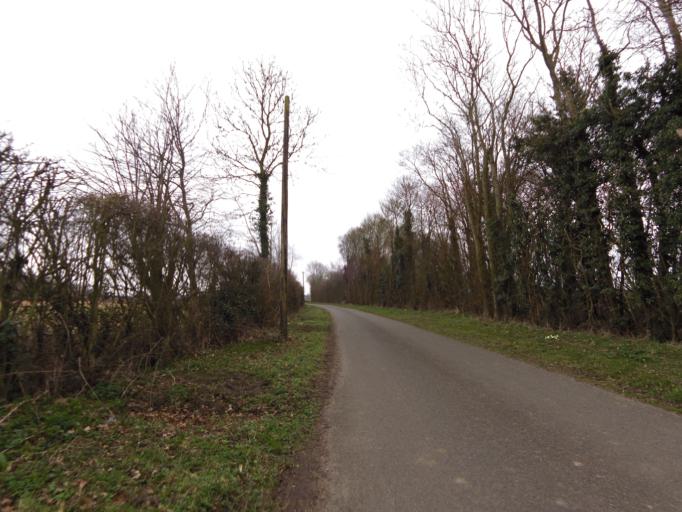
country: GB
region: England
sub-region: Suffolk
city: Halesworth
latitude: 52.3783
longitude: 1.5179
